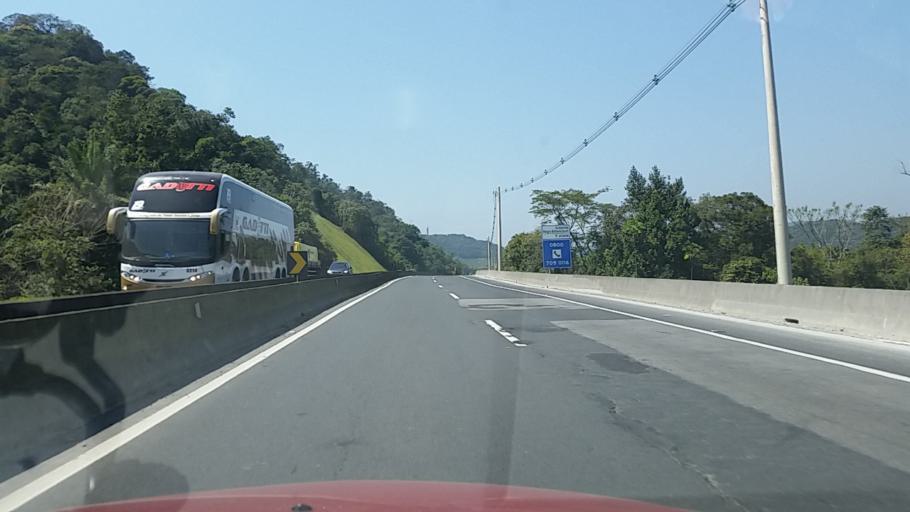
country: BR
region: Sao Paulo
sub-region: Miracatu
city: Miracatu
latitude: -24.1435
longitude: -47.2841
